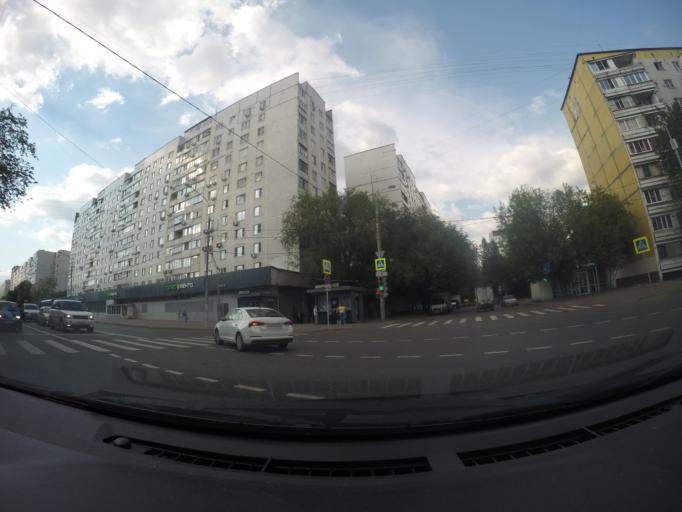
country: RU
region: Moscow
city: Kozeyevo
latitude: 55.8568
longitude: 37.6106
